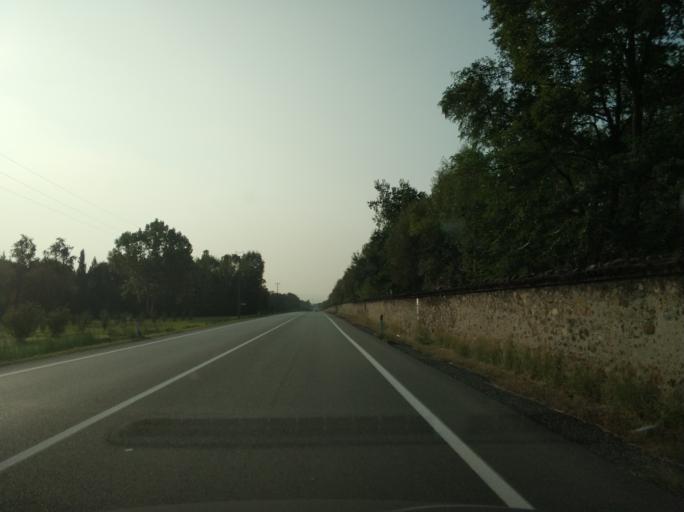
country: IT
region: Piedmont
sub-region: Provincia di Torino
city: Robassomero
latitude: 45.2027
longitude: 7.5545
